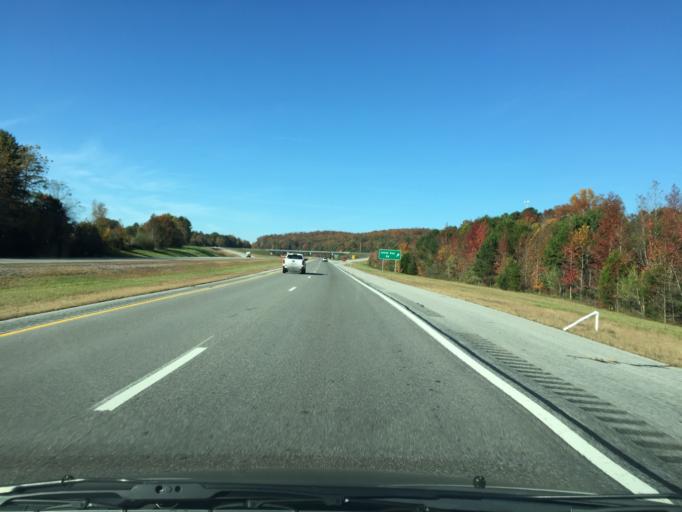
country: US
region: Tennessee
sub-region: Hamilton County
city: Sale Creek
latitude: 35.3453
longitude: -85.1754
